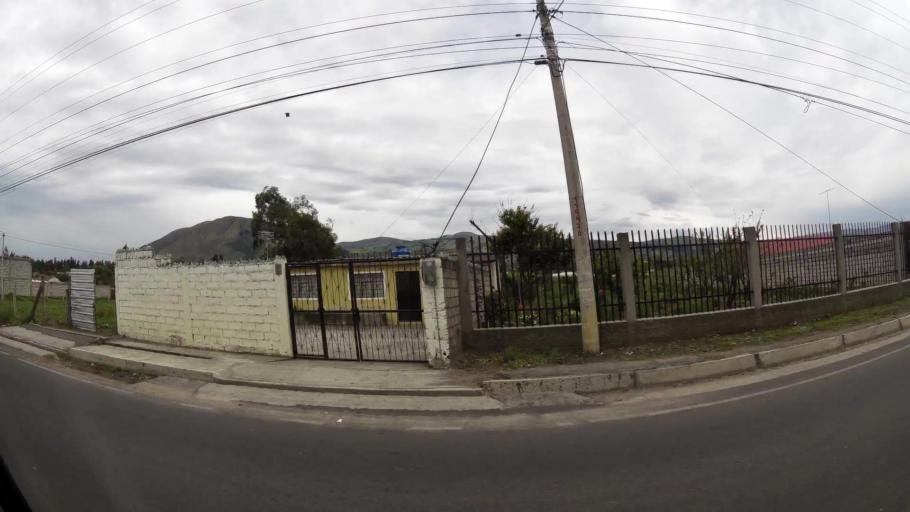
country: EC
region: Cotopaxi
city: San Miguel de Salcedo
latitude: -1.0002
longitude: -78.5938
